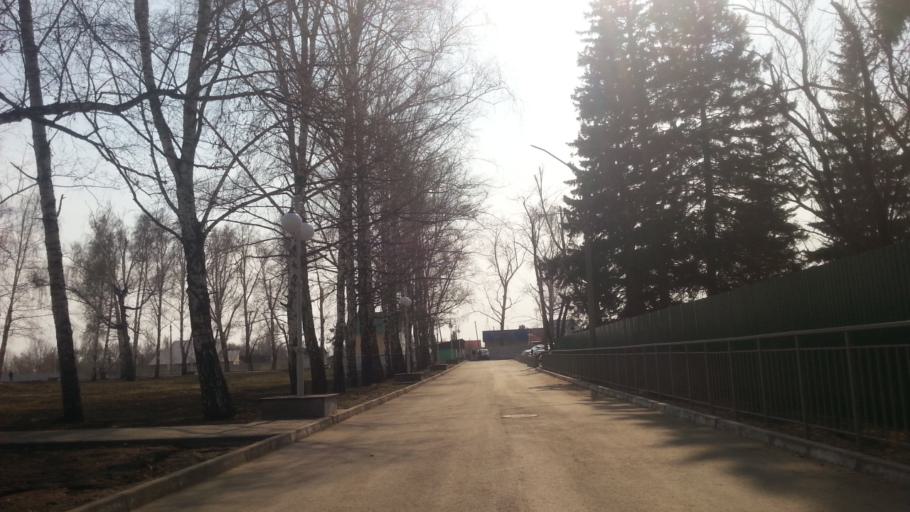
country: RU
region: Altai Krai
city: Zaton
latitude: 53.3221
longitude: 83.7942
